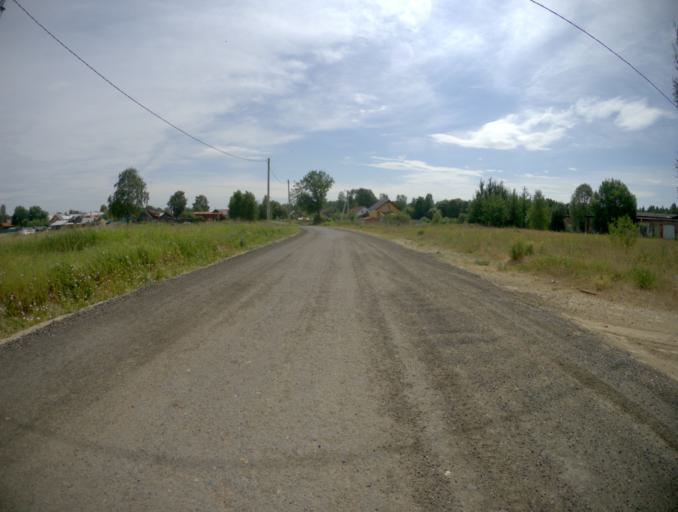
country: RU
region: Vladimir
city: Raduzhnyy
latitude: 56.0260
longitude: 40.3098
